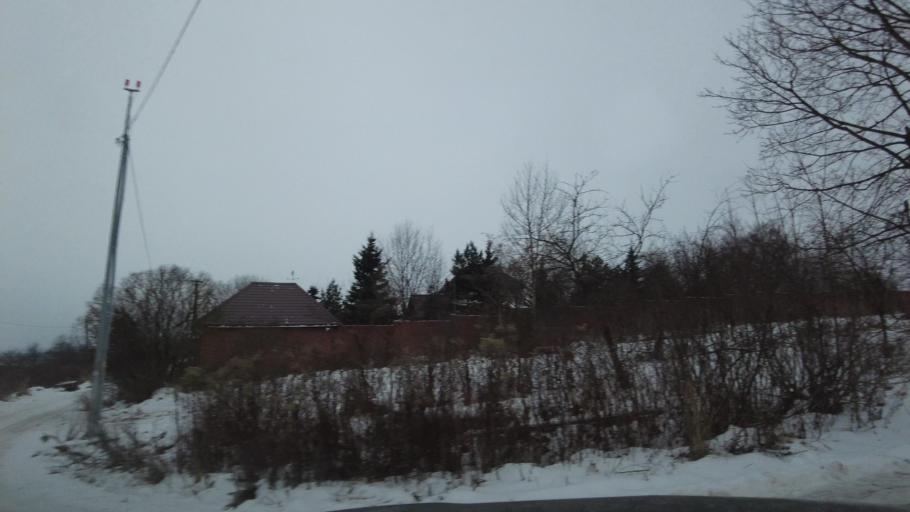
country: RU
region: Moskovskaya
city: Novopodrezkovo
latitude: 55.9908
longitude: 37.3923
